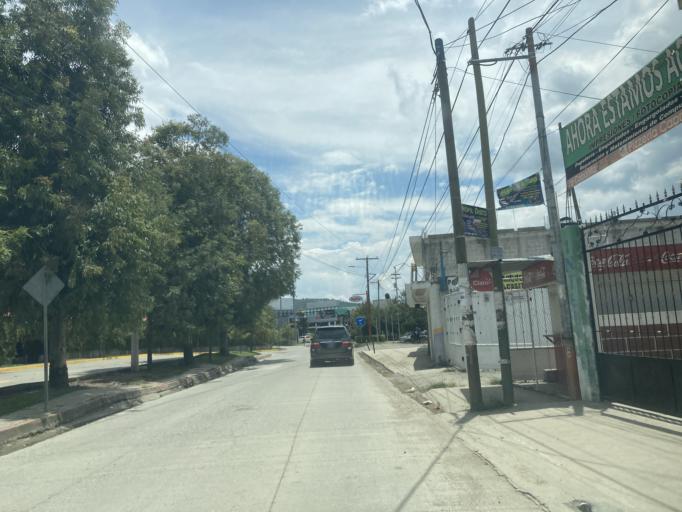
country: GT
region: Huehuetenango
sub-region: Municipio de Huehuetenango
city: Huehuetenango
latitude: 15.3224
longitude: -91.4953
